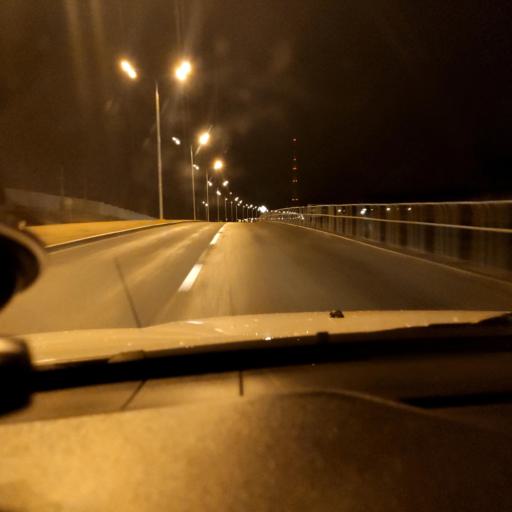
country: RU
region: Samara
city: Samara
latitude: 53.2836
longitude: 50.2387
